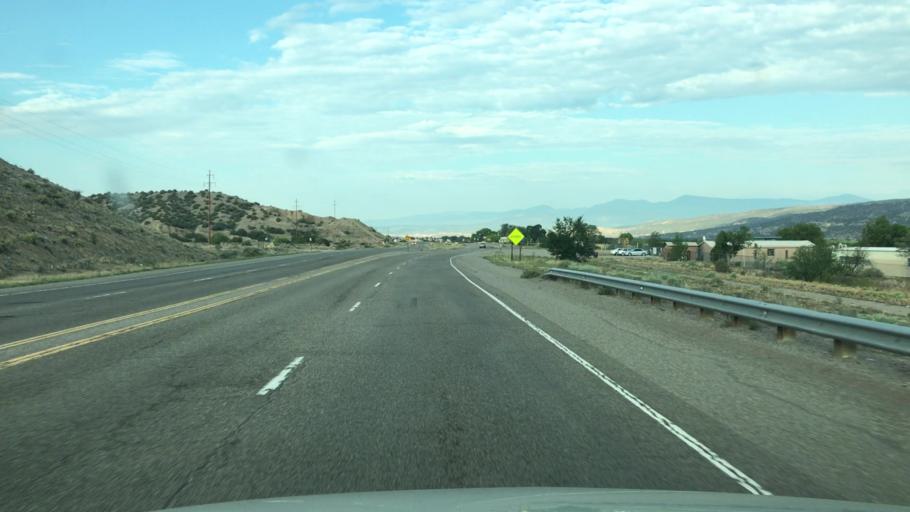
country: US
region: New Mexico
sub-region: Rio Arriba County
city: Ohkay Owingeh
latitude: 36.1483
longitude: -105.9789
